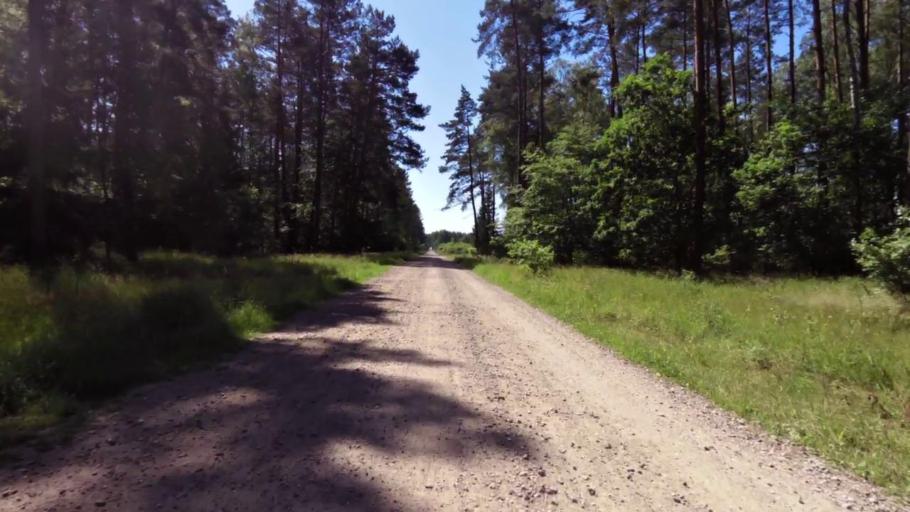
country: PL
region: West Pomeranian Voivodeship
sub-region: Powiat swidwinski
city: Rabino
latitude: 53.9005
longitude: 16.0081
